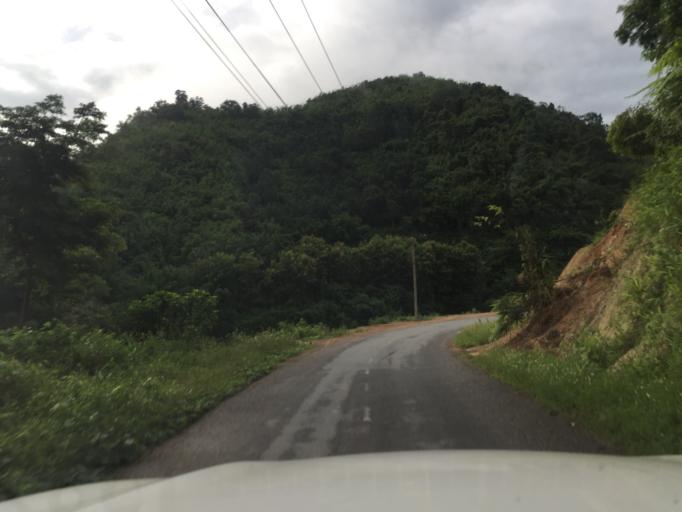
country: LA
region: Oudomxai
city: Muang La
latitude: 21.0708
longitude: 102.2412
